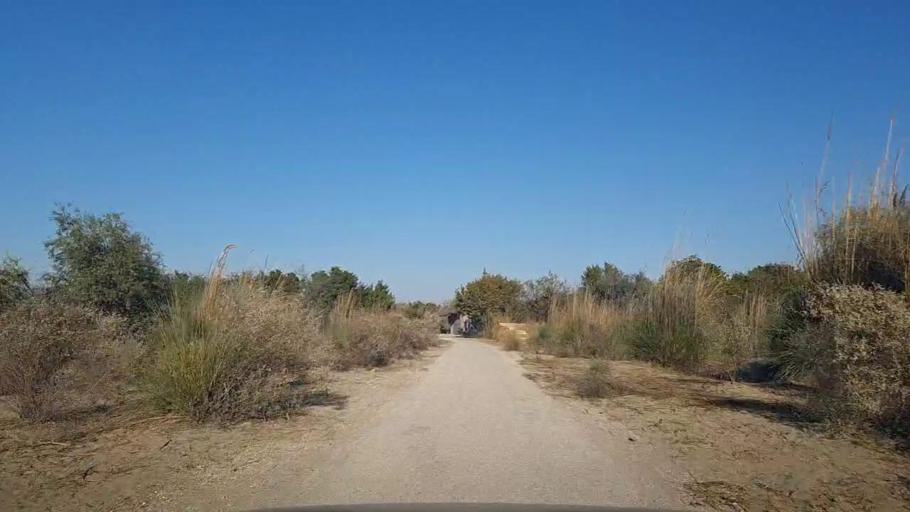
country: PK
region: Sindh
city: Khadro
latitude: 26.2531
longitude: 68.8665
